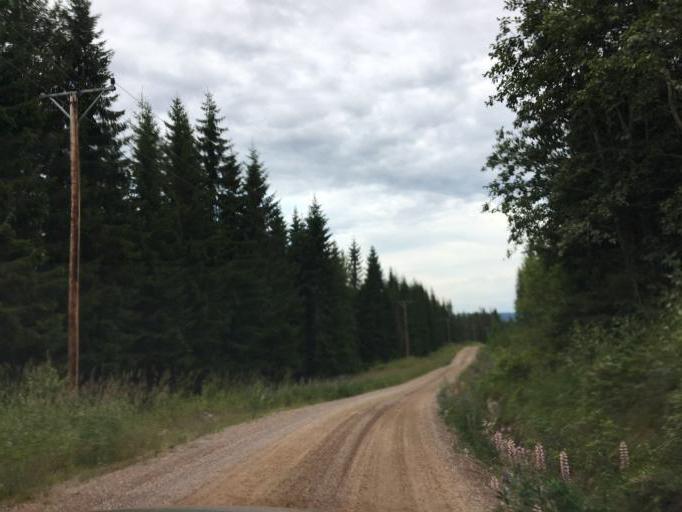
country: SE
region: Vaermland
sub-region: Filipstads Kommun
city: Lesjofors
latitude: 60.1837
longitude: 14.4010
